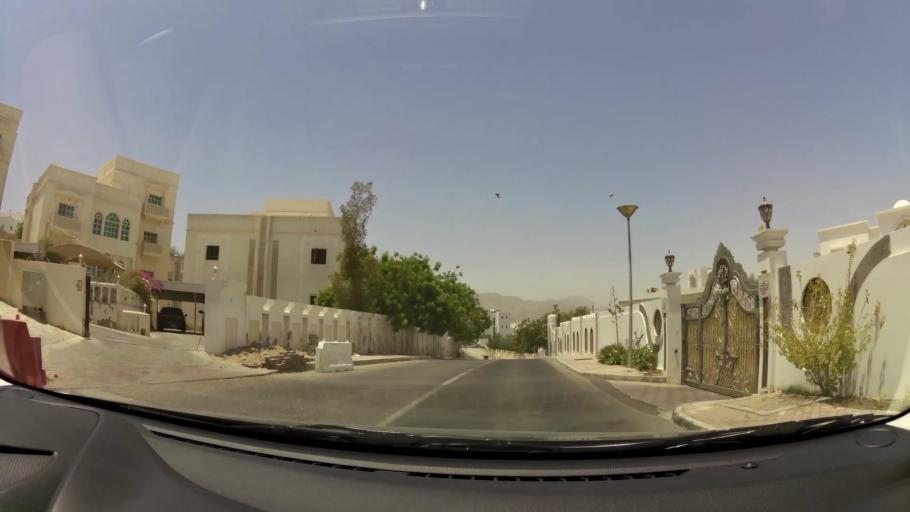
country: OM
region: Muhafazat Masqat
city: Bawshar
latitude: 23.6095
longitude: 58.4659
